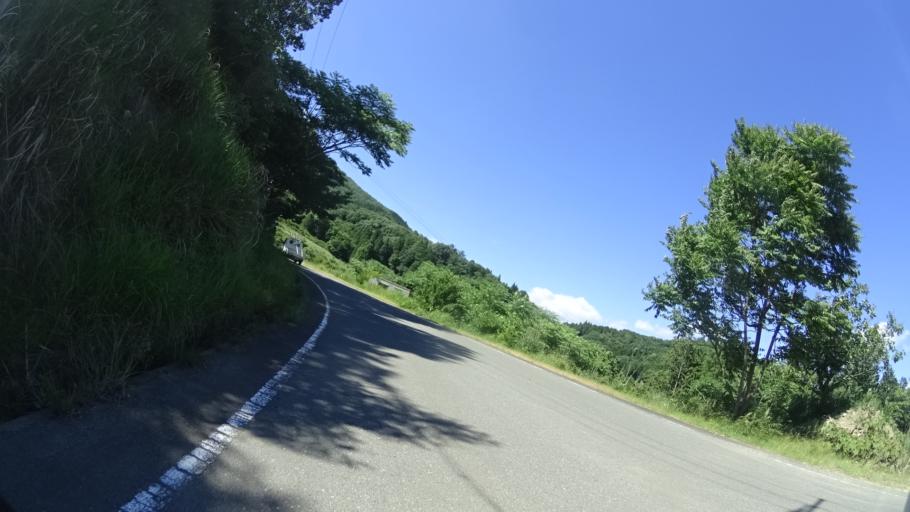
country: JP
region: Kyoto
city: Fukuchiyama
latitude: 35.3861
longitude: 135.0691
